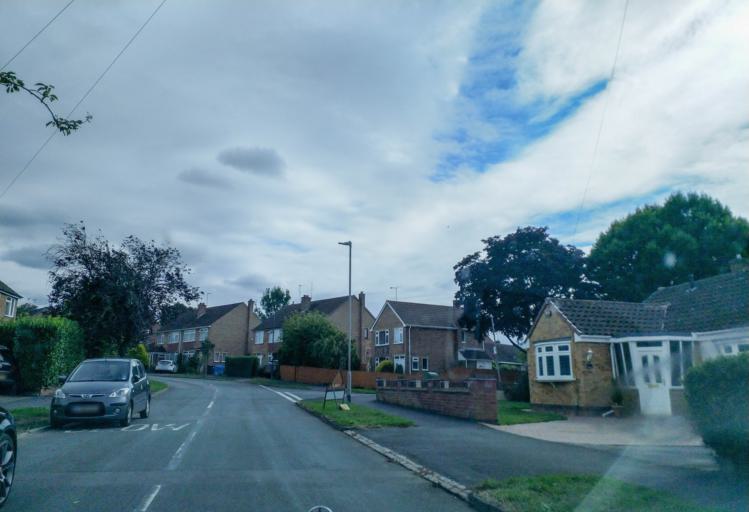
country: GB
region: England
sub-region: Warwickshire
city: Kenilworth
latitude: 52.3407
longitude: -1.5836
